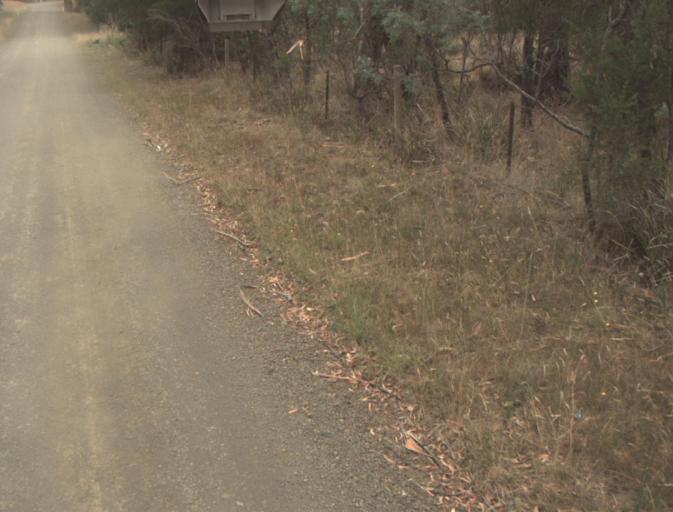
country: AU
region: Tasmania
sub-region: Northern Midlands
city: Evandale
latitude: -41.5282
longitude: 147.3583
